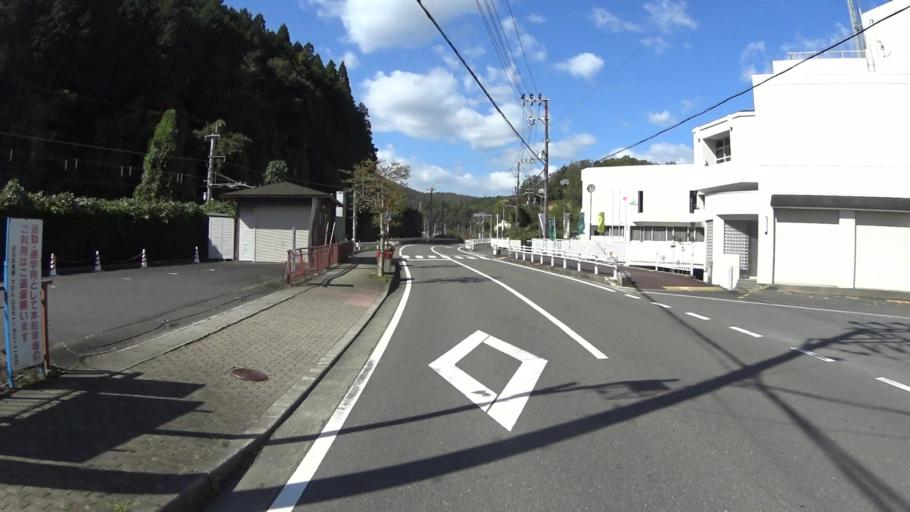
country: JP
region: Kyoto
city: Kameoka
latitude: 35.1637
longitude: 135.5025
